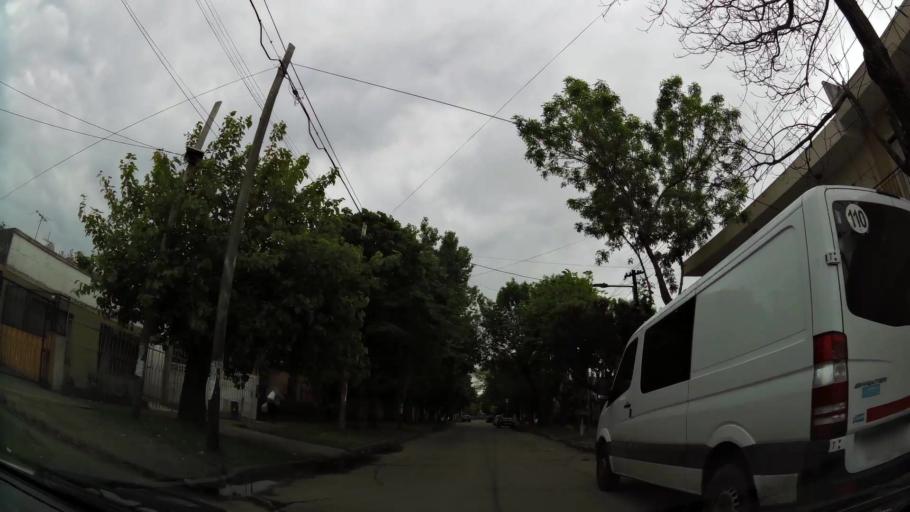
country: AR
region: Buenos Aires
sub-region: Partido de Quilmes
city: Quilmes
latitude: -34.7992
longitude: -58.2768
